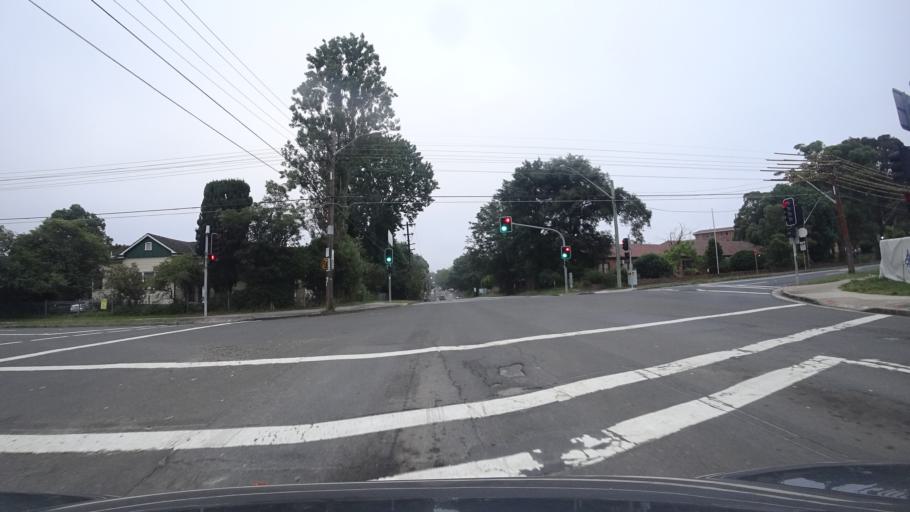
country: AU
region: New South Wales
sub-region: Ku-ring-gai
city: Normanhurst
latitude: -33.7360
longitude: 151.1002
